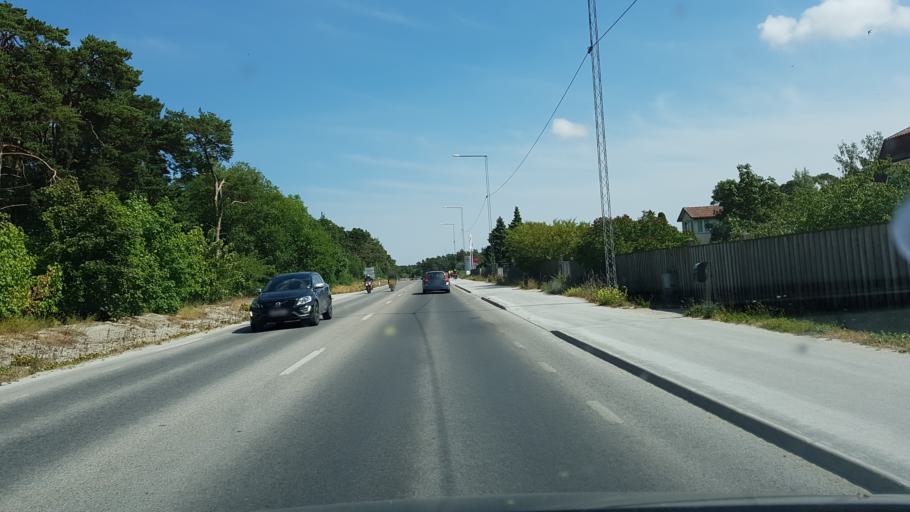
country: SE
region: Gotland
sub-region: Gotland
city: Visby
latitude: 57.6311
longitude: 18.3382
